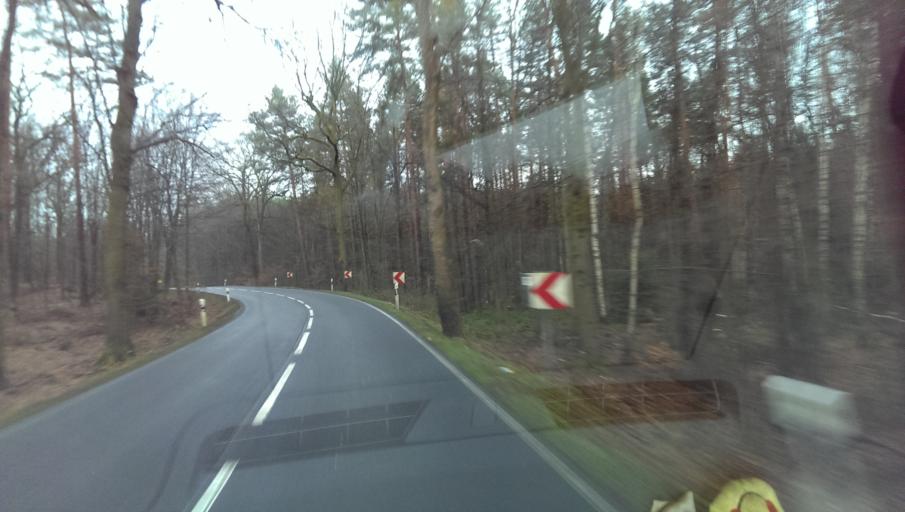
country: DE
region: Saxony
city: Coswig
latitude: 51.1655
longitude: 13.6252
